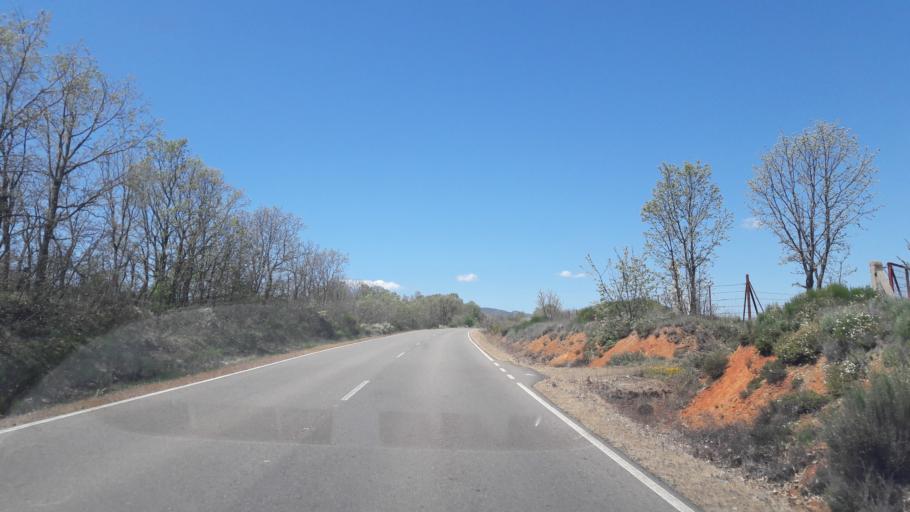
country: ES
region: Castille and Leon
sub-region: Provincia de Salamanca
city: Monleon
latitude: 40.5915
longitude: -5.8764
